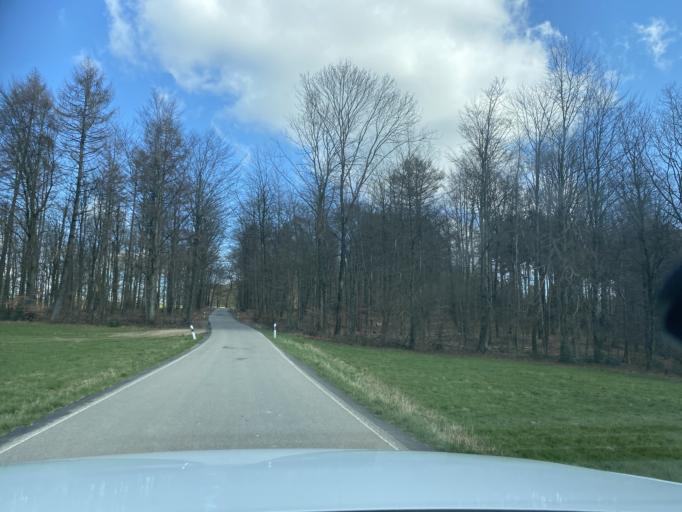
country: DE
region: North Rhine-Westphalia
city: Wipperfurth
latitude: 51.1530
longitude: 7.4125
